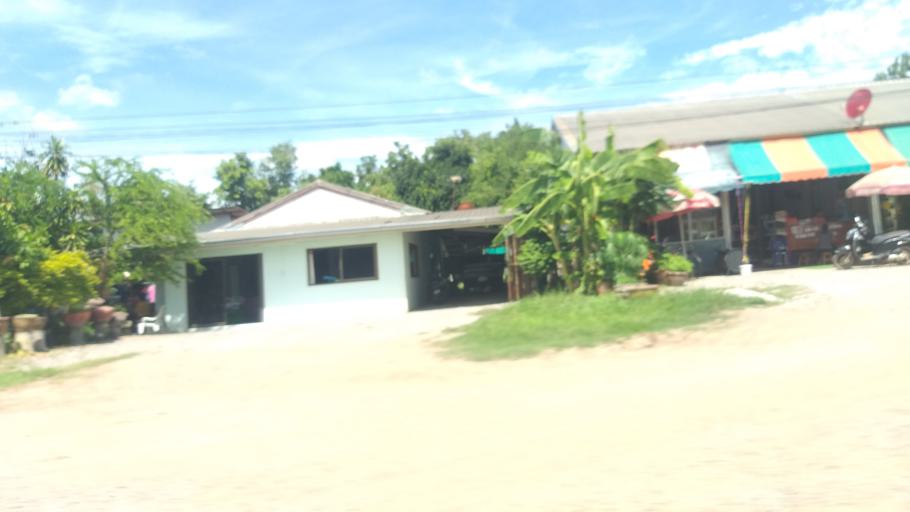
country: TH
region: Khon Kaen
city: Nong Ruea
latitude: 16.4851
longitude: 102.4357
